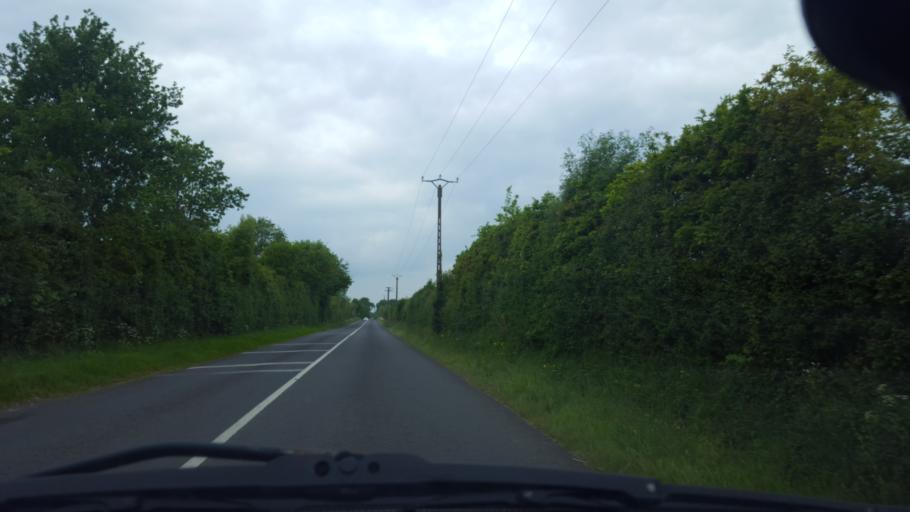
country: FR
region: Pays de la Loire
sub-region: Departement de la Loire-Atlantique
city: La Limouziniere
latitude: 47.0121
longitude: -1.6195
